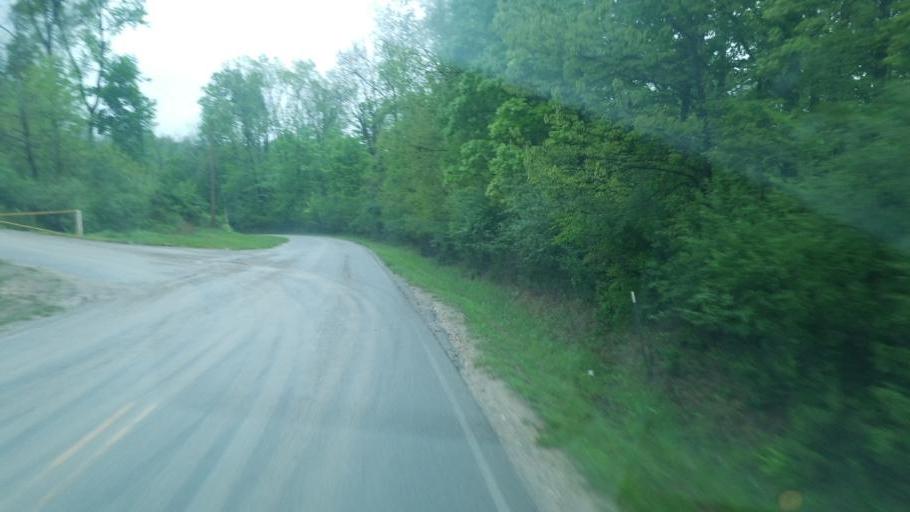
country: US
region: Ohio
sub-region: Highland County
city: Hillsboro
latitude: 39.1752
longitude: -83.6403
